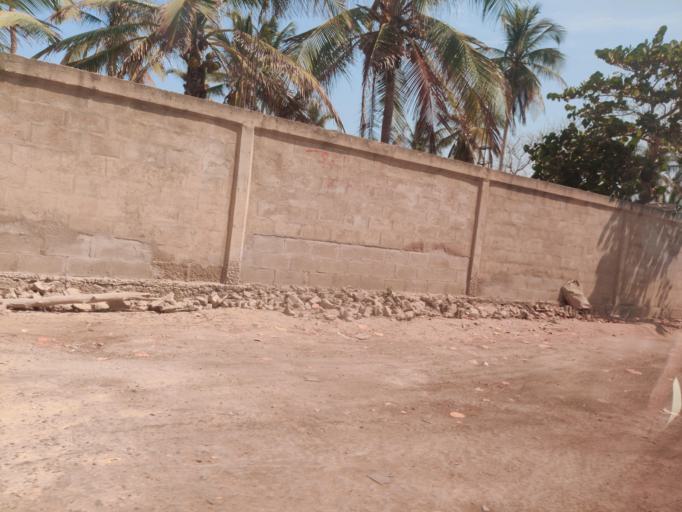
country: CO
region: Bolivar
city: Turbana
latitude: 10.1910
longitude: -75.6323
